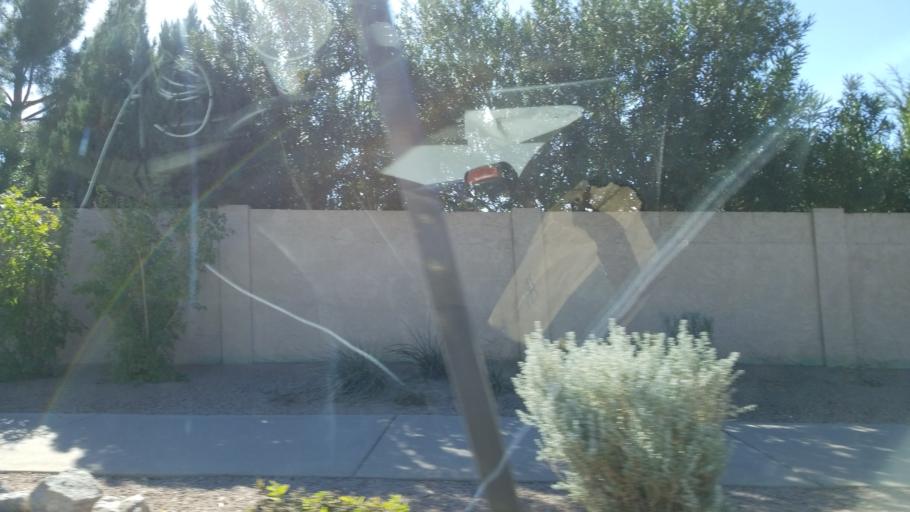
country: US
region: Arizona
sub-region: Maricopa County
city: Paradise Valley
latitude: 33.5593
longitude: -111.9083
